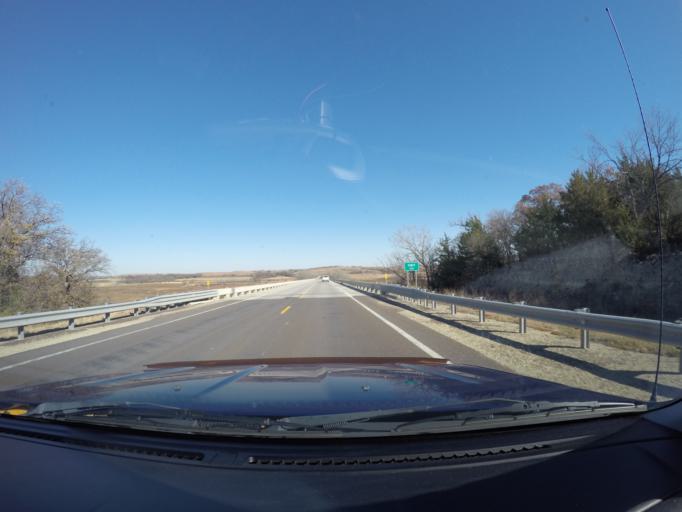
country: US
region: Kansas
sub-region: Marshall County
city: Blue Rapids
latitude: 39.4635
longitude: -96.7588
